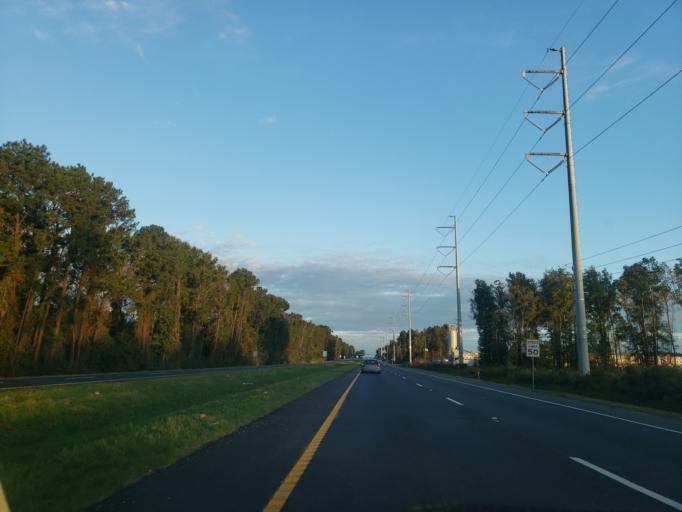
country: US
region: Georgia
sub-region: Chatham County
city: Port Wentworth
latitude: 32.1382
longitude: -81.1745
